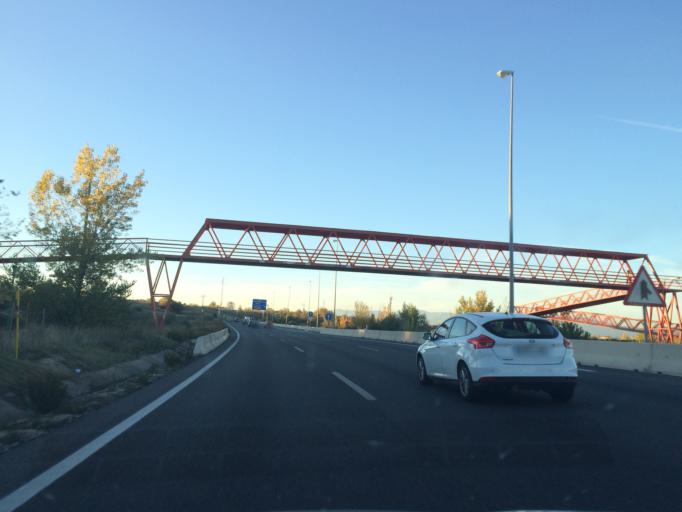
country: ES
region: Madrid
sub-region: Provincia de Madrid
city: Las Tablas
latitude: 40.5405
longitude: -3.6976
